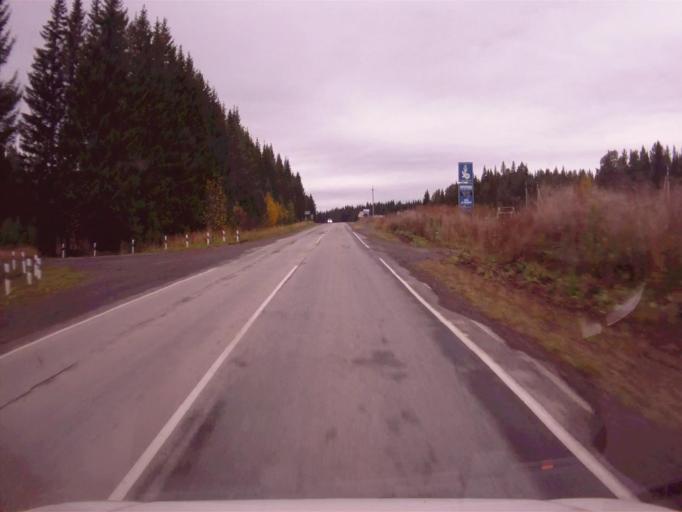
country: RU
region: Chelyabinsk
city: Nyazepetrovsk
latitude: 56.0660
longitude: 59.6512
